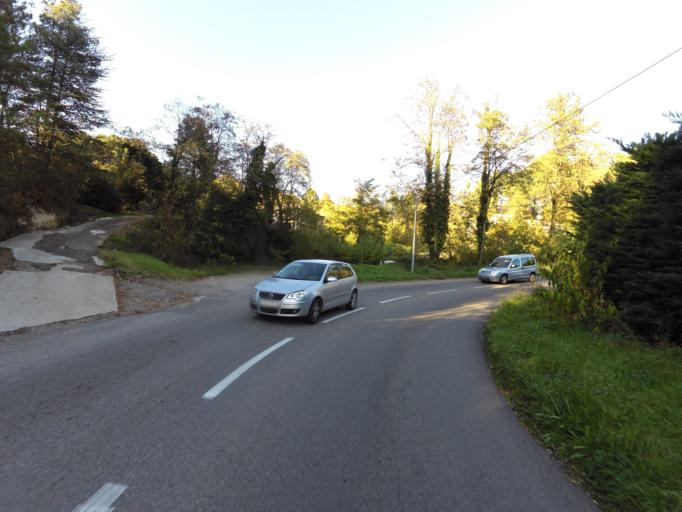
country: FR
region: Rhone-Alpes
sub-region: Departement de l'Ardeche
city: Joyeuse
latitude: 44.4891
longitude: 4.2298
